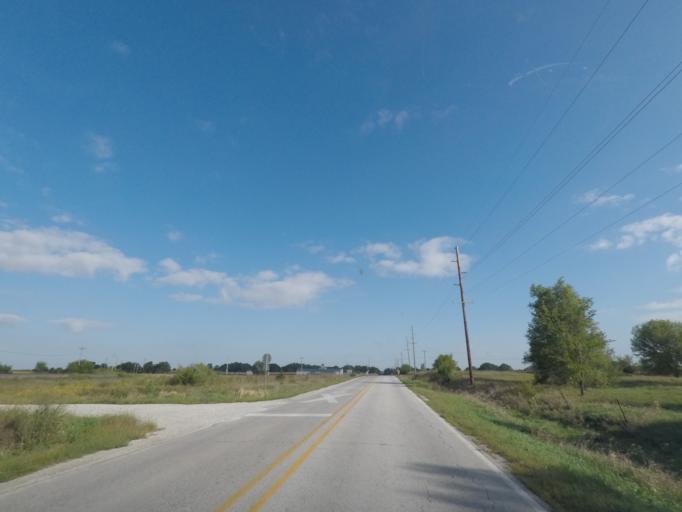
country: US
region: Iowa
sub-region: Story County
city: Nevada
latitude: 42.0096
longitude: -93.4628
